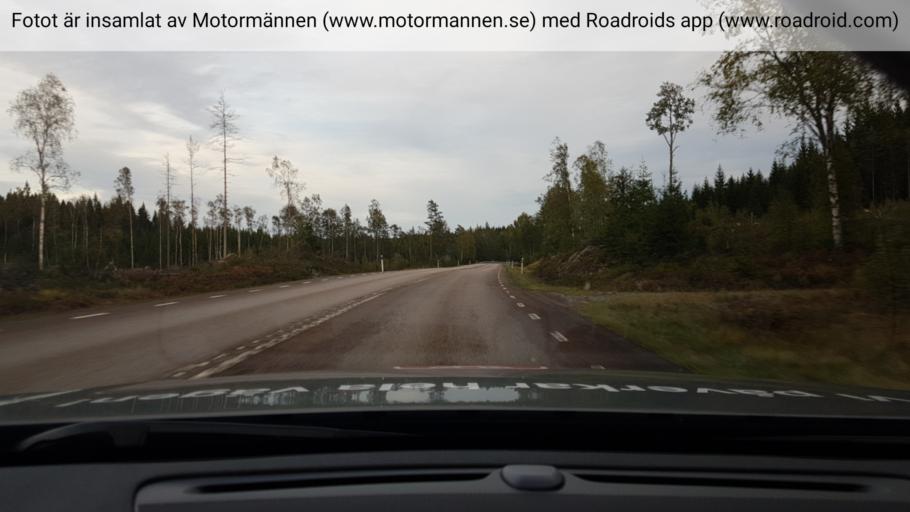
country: SE
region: Vaestra Goetaland
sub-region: Amals Kommun
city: Amal
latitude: 59.0610
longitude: 12.5189
